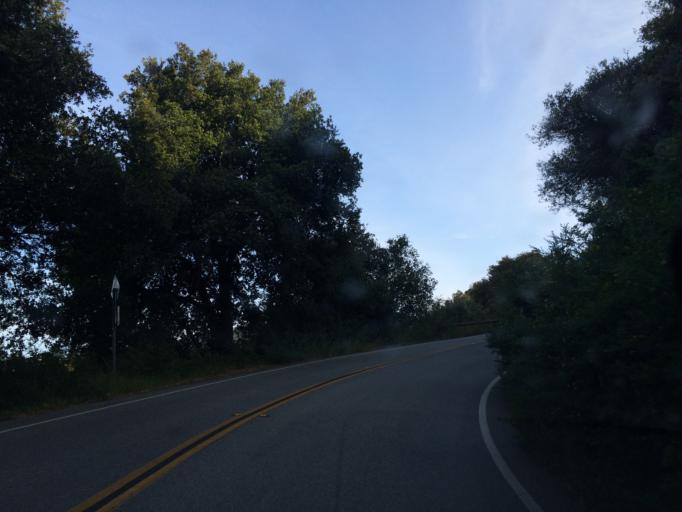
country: US
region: California
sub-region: Santa Clara County
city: Los Altos Hills
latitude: 37.3481
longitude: -122.1758
